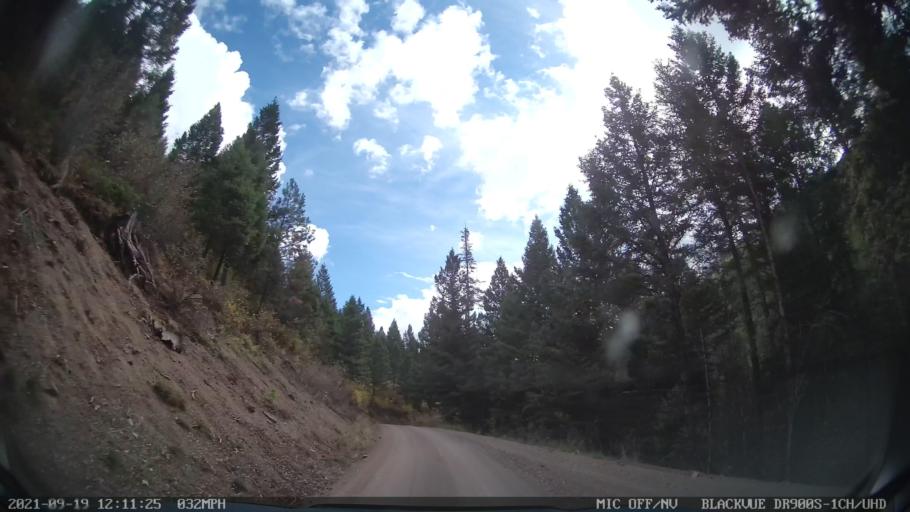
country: US
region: Montana
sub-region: Missoula County
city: Seeley Lake
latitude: 47.1745
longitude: -113.3739
